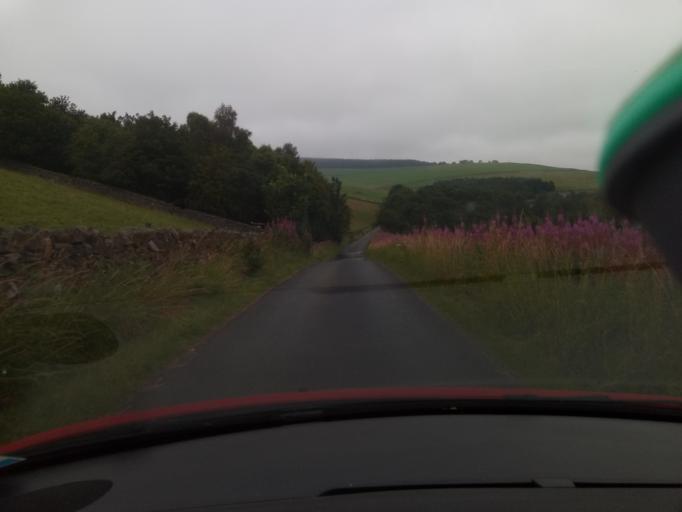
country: GB
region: Scotland
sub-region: The Scottish Borders
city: Galashiels
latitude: 55.7008
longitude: -2.8910
